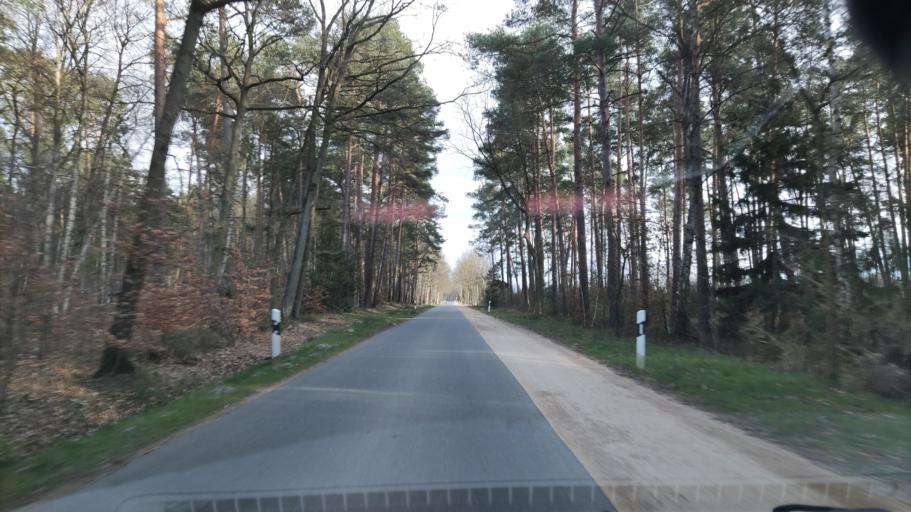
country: DE
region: Lower Saxony
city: Langendorf
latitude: 53.0349
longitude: 11.2578
